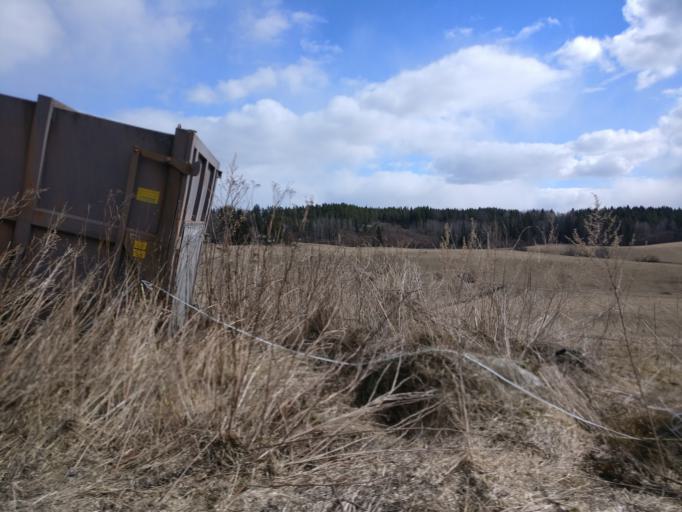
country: FI
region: Uusimaa
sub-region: Helsinki
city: Karjalohja
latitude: 60.2078
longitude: 23.7331
